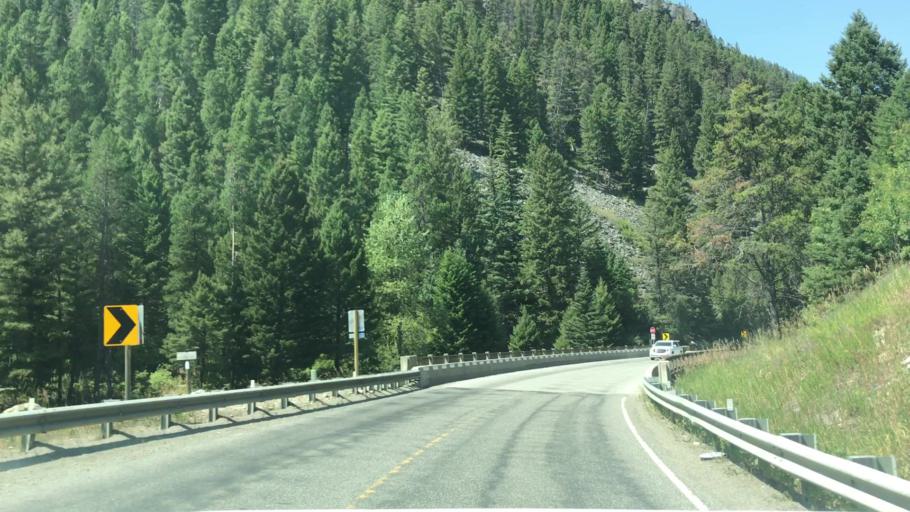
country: US
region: Montana
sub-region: Gallatin County
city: Big Sky
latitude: 45.4074
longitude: -111.2255
